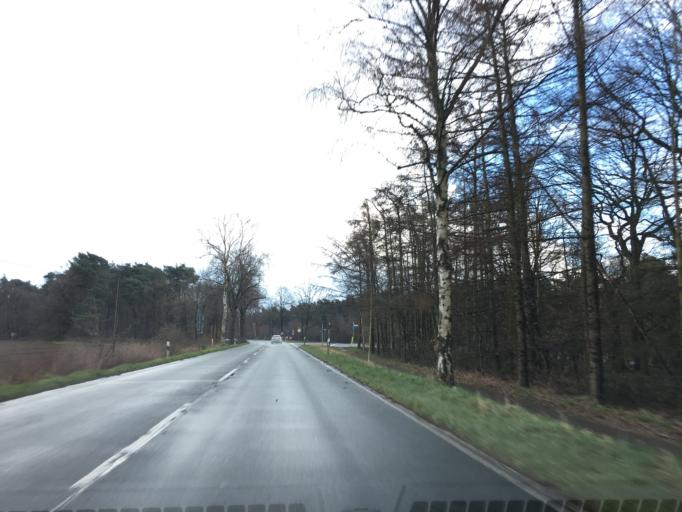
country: DE
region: North Rhine-Westphalia
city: Olfen
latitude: 51.7356
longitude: 7.3013
